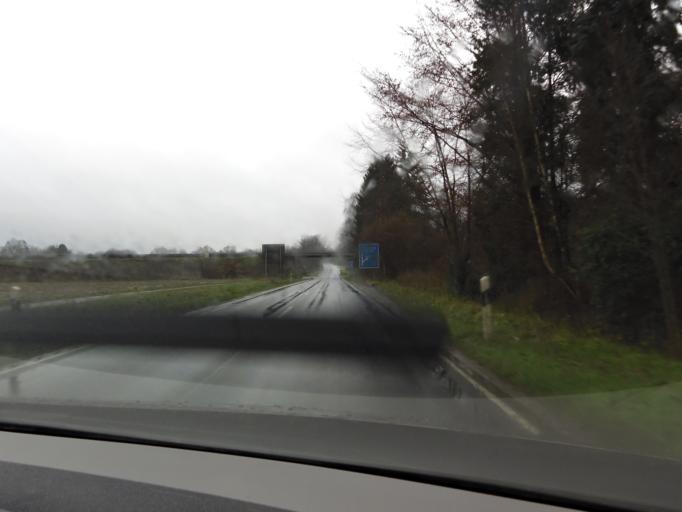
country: DE
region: Lower Saxony
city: Bad Fallingbostel
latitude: 52.8946
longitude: 9.7645
